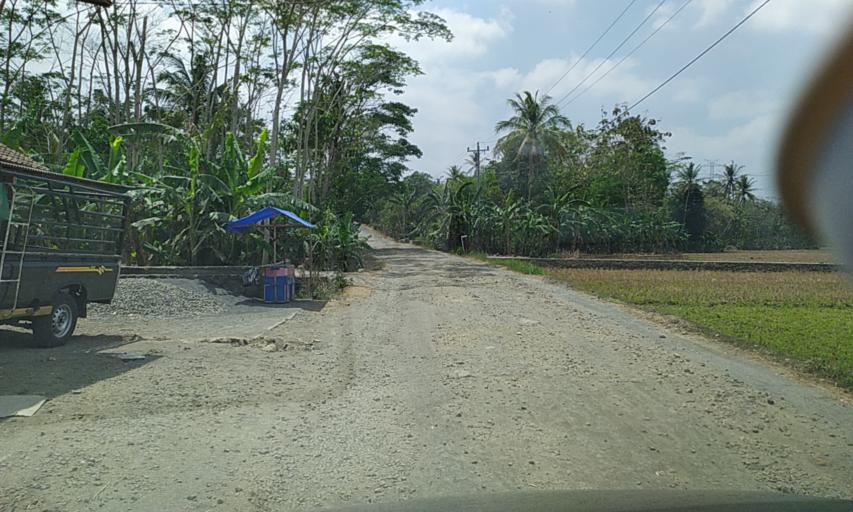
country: ID
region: Central Java
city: Prapagan
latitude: -7.5840
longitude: 108.9507
